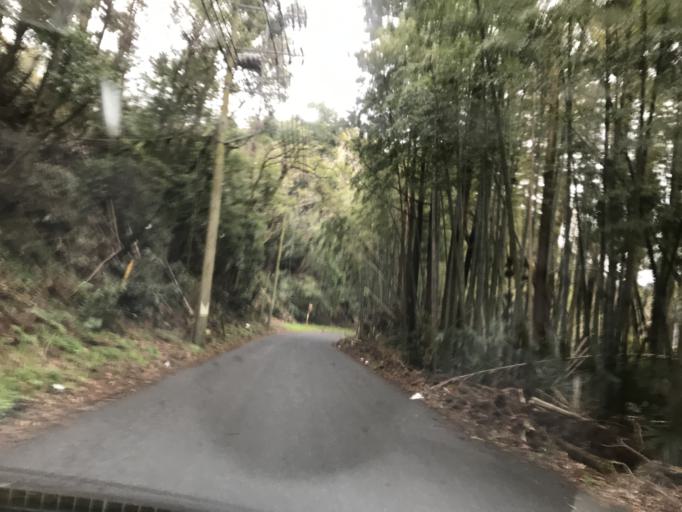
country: JP
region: Chiba
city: Sawara
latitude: 35.8516
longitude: 140.5320
